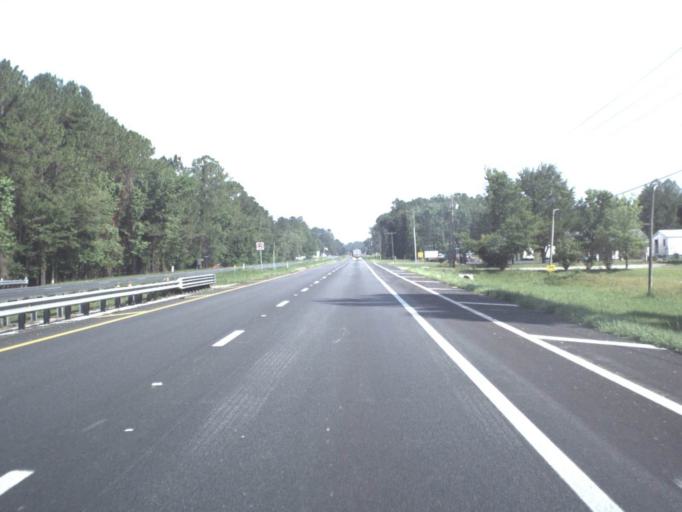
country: US
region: Florida
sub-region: Nassau County
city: Callahan
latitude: 30.5415
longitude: -81.8137
